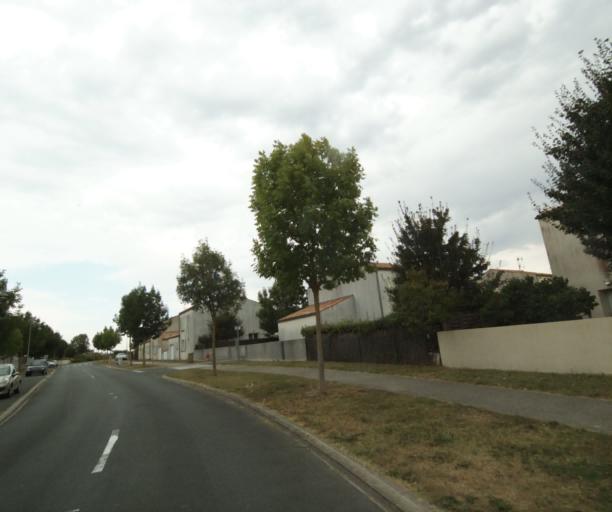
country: FR
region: Poitou-Charentes
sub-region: Departement de la Charente-Maritime
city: Tonnay-Charente
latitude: 45.9484
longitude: -0.8958
